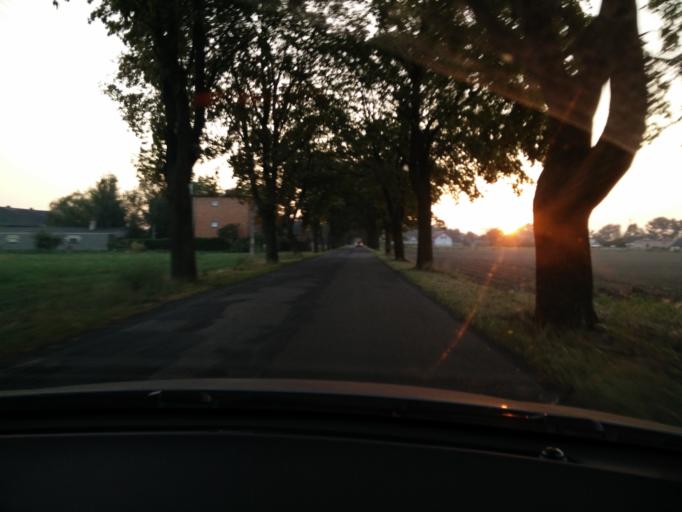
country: PL
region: Greater Poland Voivodeship
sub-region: Powiat sredzki
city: Dominowo
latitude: 52.2135
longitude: 17.3905
